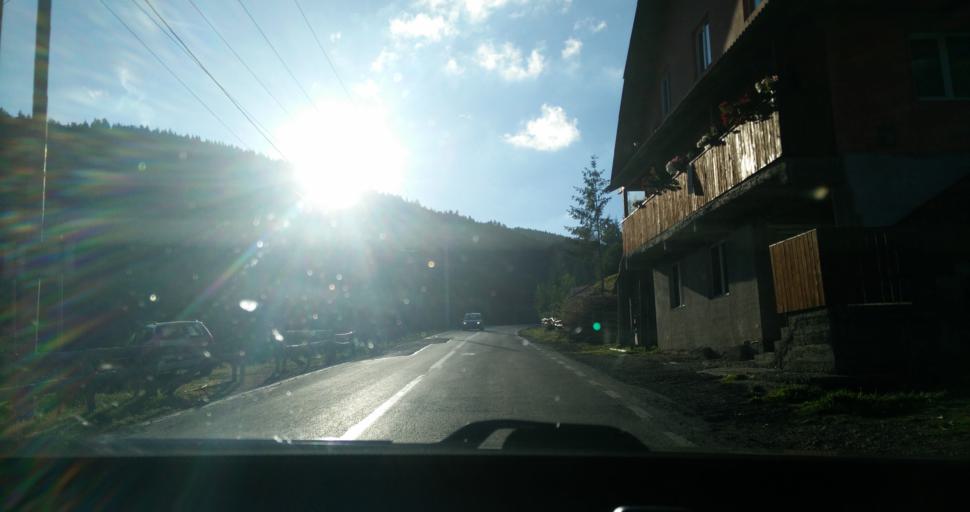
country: RO
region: Alba
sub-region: Comuna Arieseni
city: Arieseni
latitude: 46.5066
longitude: 22.6986
